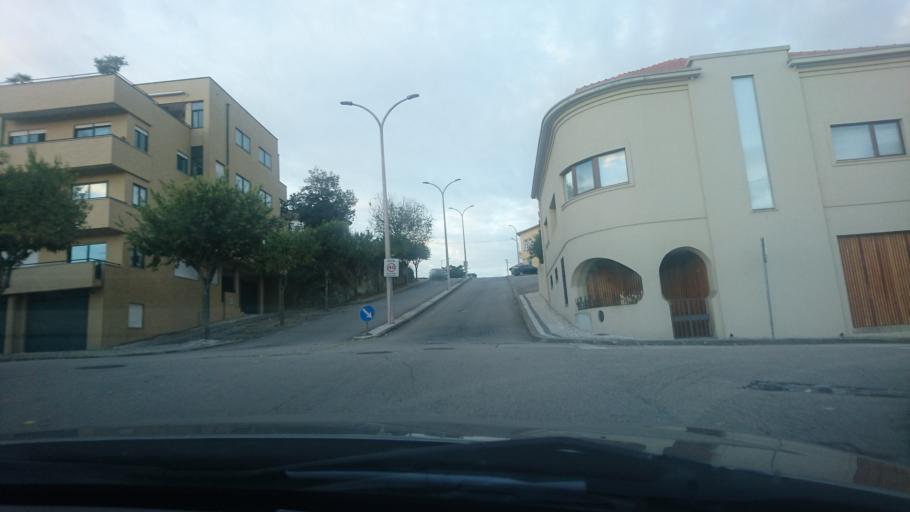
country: PT
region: Aveiro
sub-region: Sao Joao da Madeira
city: Sao Joao da Madeira
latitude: 40.8935
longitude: -8.4883
